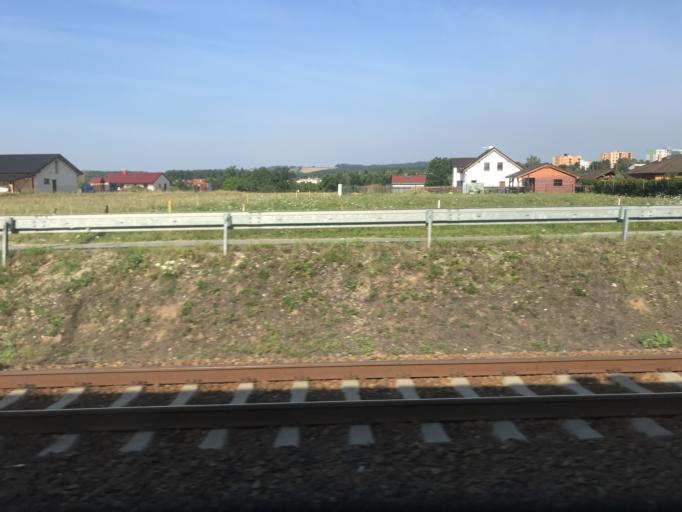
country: CZ
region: Jihocesky
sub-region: Okres Tabor
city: Sezimovo Usti
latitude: 49.3837
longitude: 14.6987
